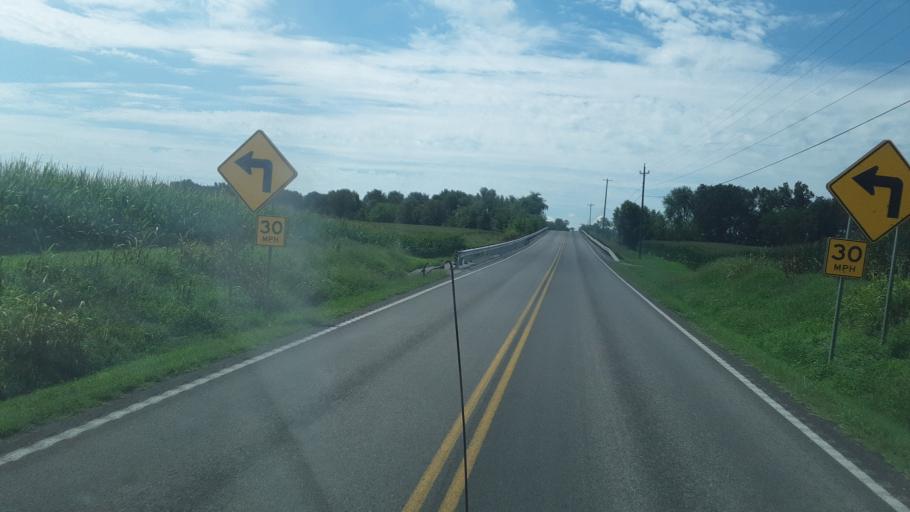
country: US
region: Kentucky
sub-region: Christian County
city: Oak Grove
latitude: 36.7586
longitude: -87.3208
